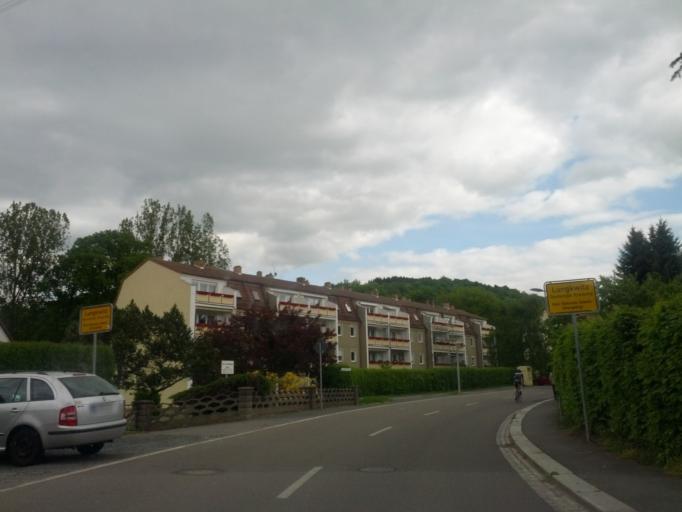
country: DE
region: Saxony
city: Kreischa
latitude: 50.9414
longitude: 13.7664
